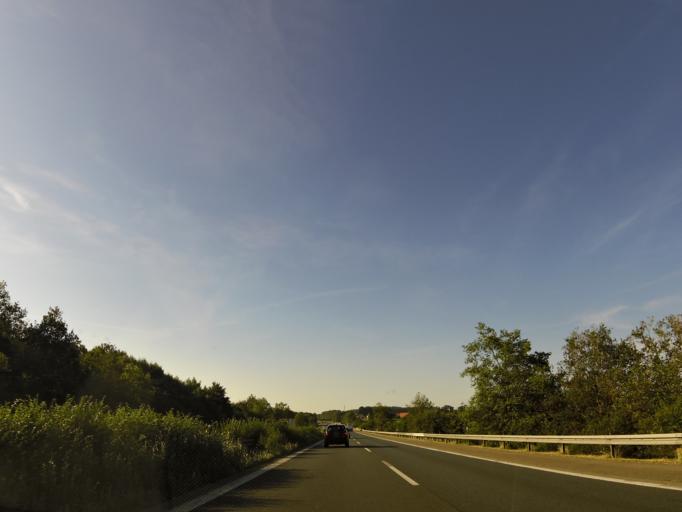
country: DE
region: Bavaria
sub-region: Regierungsbezirk Mittelfranken
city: Gremsdorf
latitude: 49.6918
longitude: 10.8591
